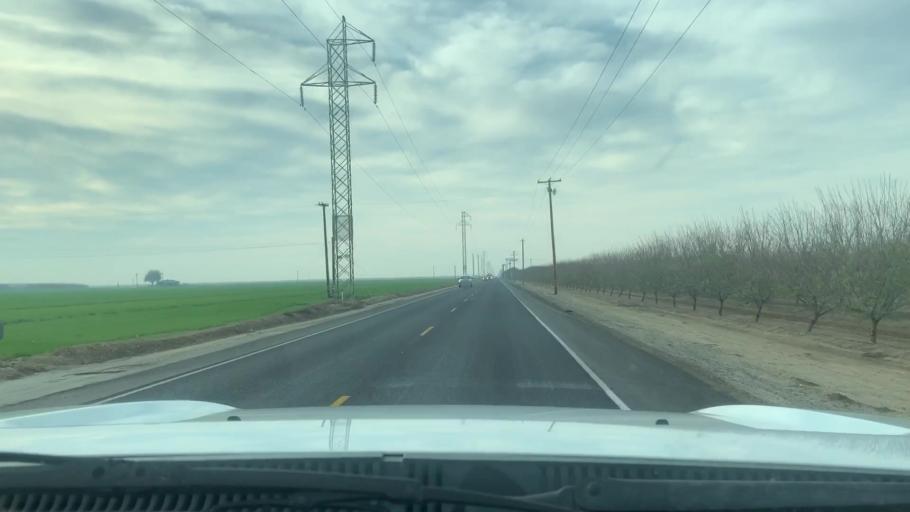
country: US
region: California
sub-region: Kern County
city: Shafter
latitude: 35.4419
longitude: -119.3096
